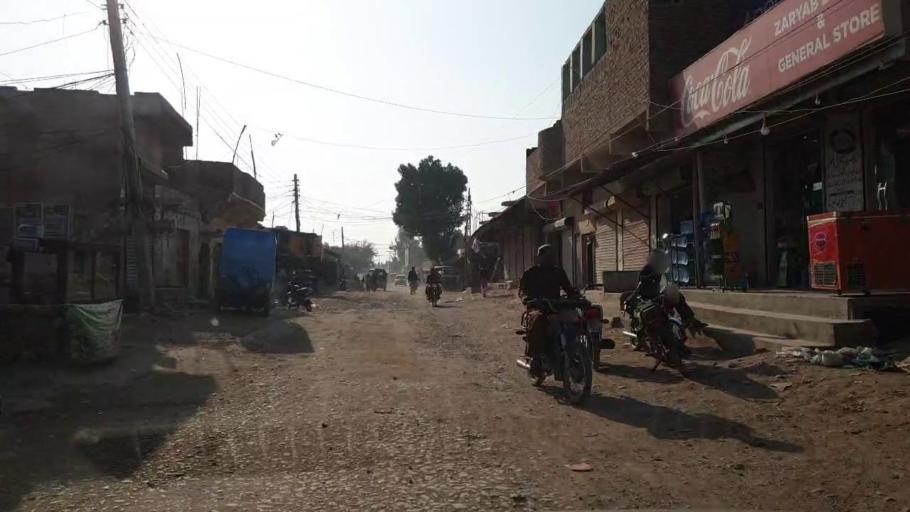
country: PK
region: Sindh
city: Kotri
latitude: 25.3575
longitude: 68.2709
